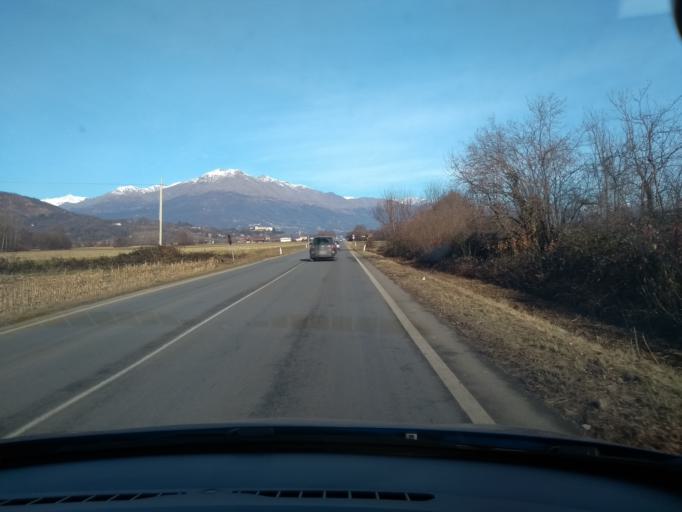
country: IT
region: Piedmont
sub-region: Provincia di Torino
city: Busano
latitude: 45.3433
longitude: 7.6559
